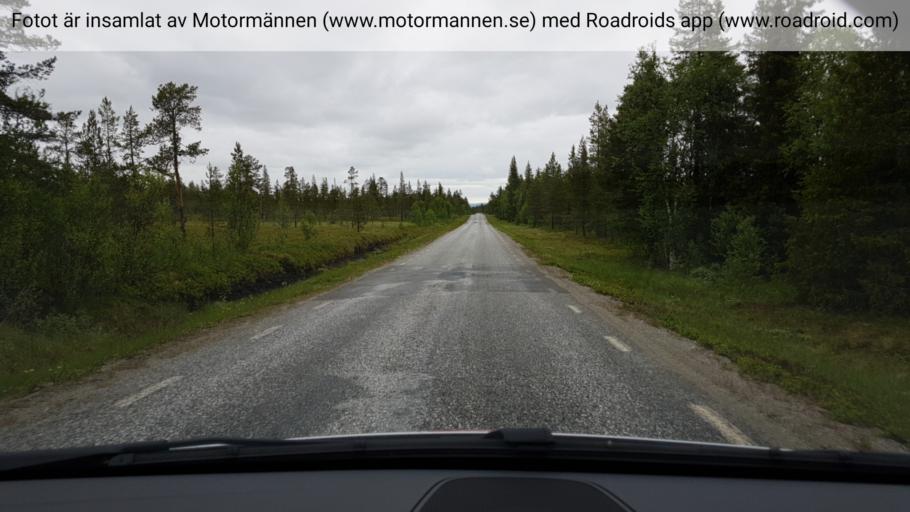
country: SE
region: Jaemtland
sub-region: Harjedalens Kommun
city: Sveg
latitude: 62.3273
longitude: 13.4212
